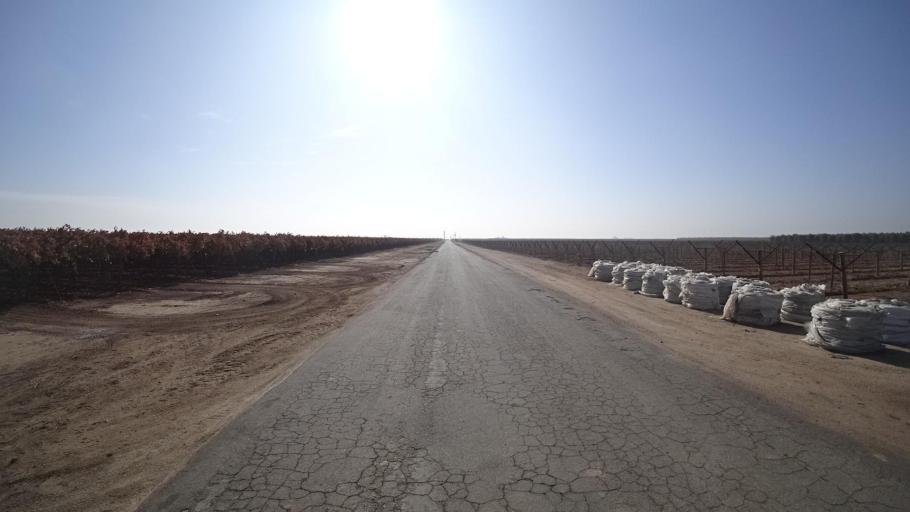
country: US
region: California
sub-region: Kern County
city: McFarland
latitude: 35.6273
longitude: -119.1866
